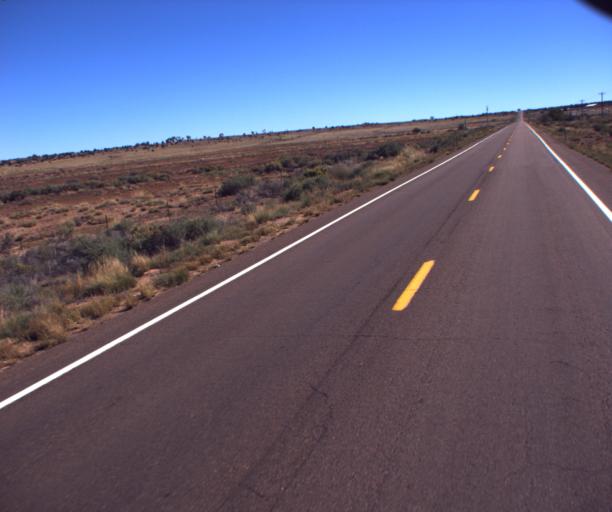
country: US
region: Arizona
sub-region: Apache County
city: Saint Johns
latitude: 34.5088
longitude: -109.4354
